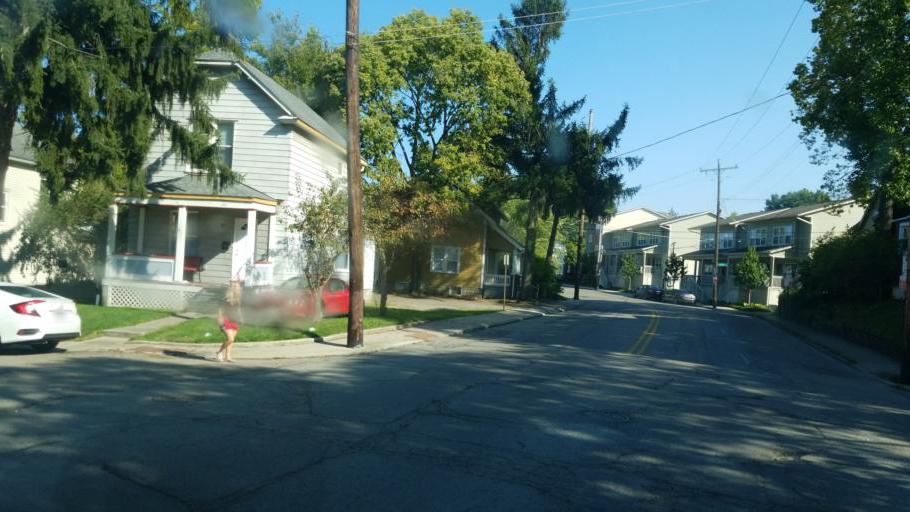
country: US
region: Ohio
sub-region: Franklin County
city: Grandview Heights
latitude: 40.0119
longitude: -83.0131
